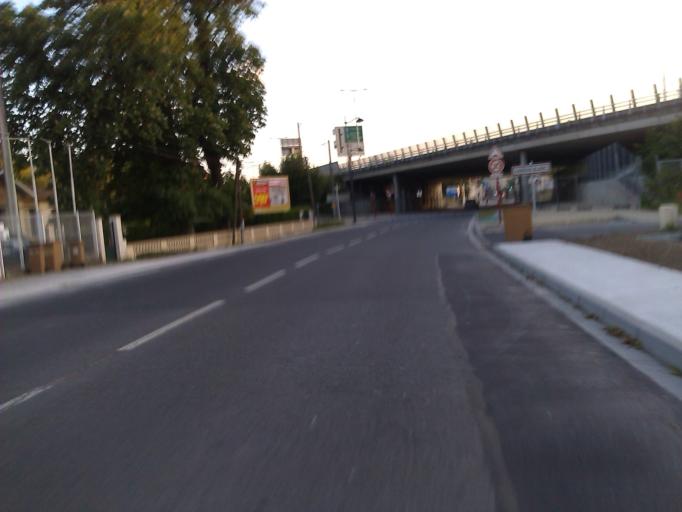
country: FR
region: Aquitaine
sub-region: Departement de la Gironde
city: Carbon-Blanc
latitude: 44.8989
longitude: -0.4943
